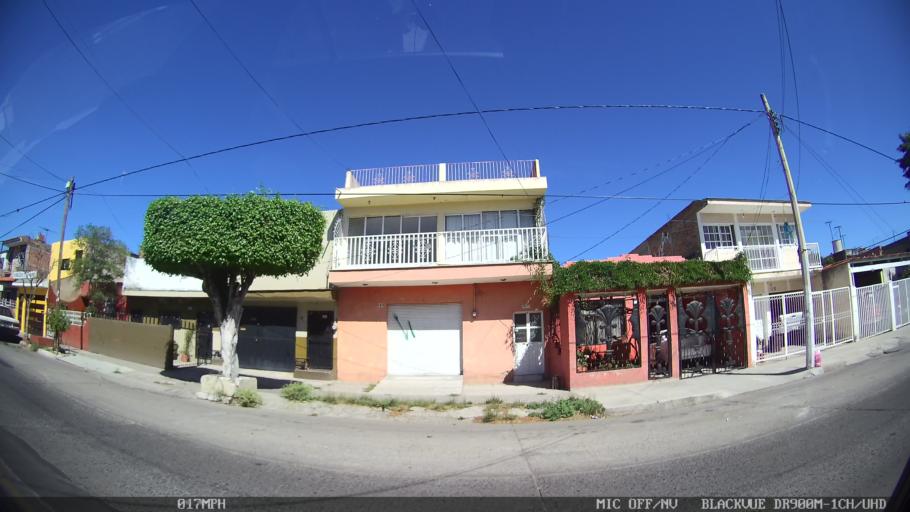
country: MX
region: Jalisco
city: Tlaquepaque
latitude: 20.6997
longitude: -103.2864
